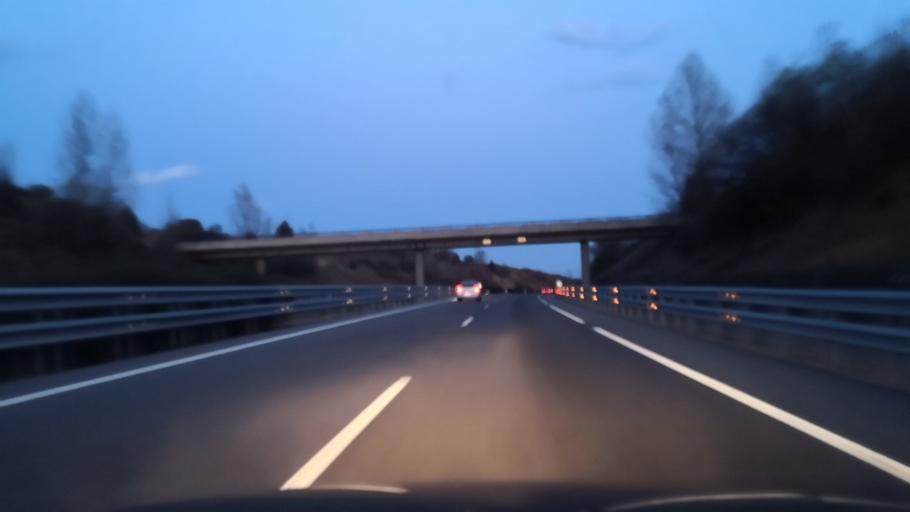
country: ES
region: Castille and Leon
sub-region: Provincia de Leon
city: Bembibre
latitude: 42.6275
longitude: -6.4177
